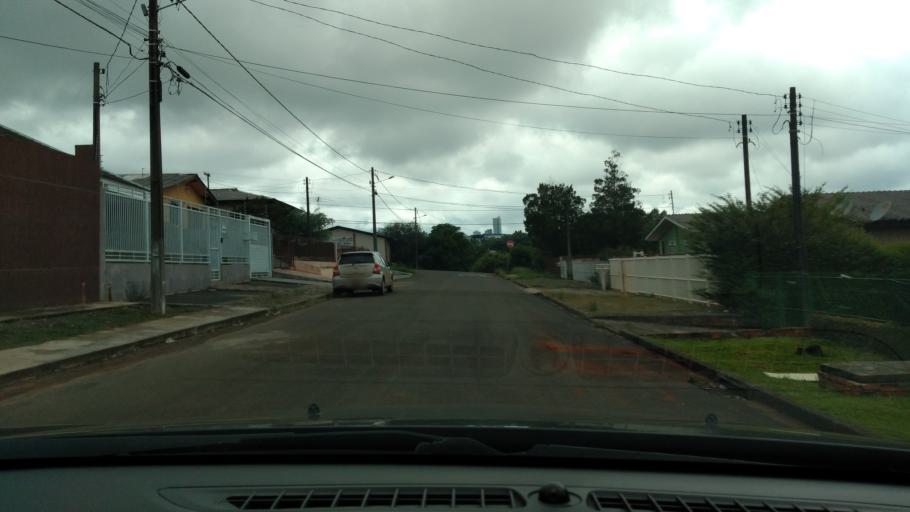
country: BR
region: Parana
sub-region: Guarapuava
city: Guarapuava
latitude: -25.3945
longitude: -51.4893
